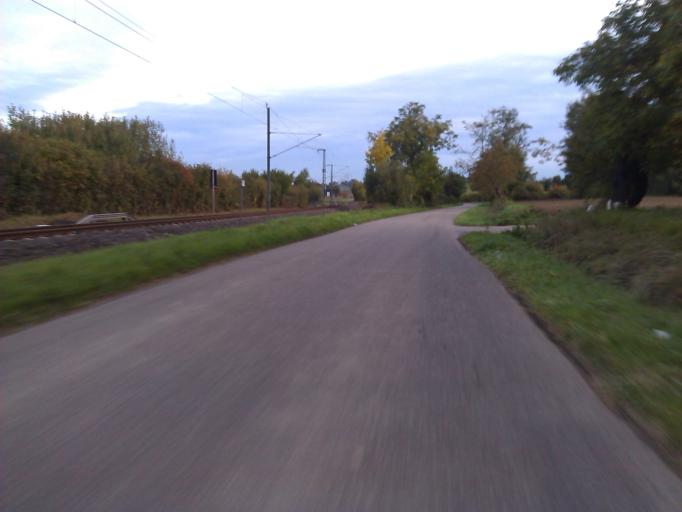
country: DE
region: Baden-Wuerttemberg
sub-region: Karlsruhe Region
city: Meckesheim
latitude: 49.3082
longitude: 8.8138
